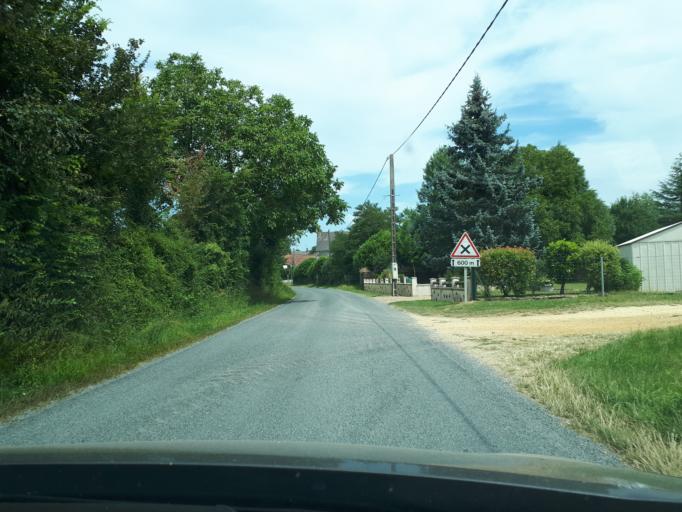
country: FR
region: Centre
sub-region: Departement du Cher
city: Sancerre
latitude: 47.2840
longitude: 2.7534
